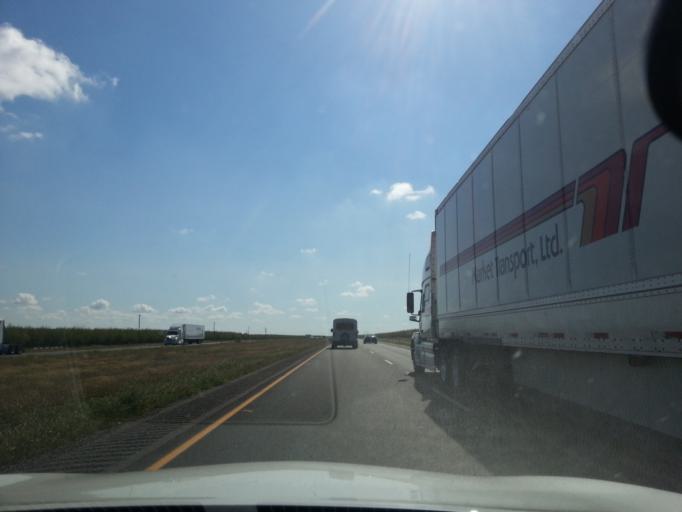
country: US
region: California
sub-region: Fresno County
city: San Joaquin
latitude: 36.4100
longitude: -120.3714
